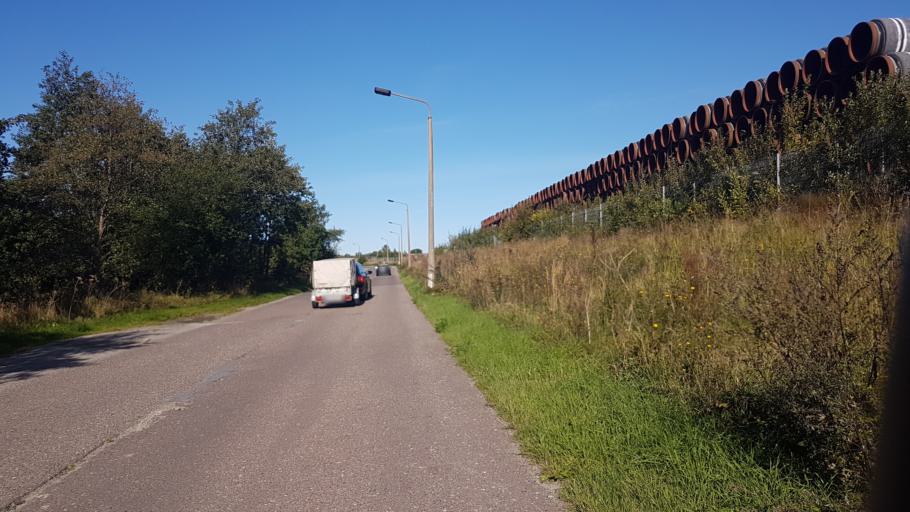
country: DE
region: Mecklenburg-Vorpommern
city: Sagard
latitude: 54.4906
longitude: 13.5713
